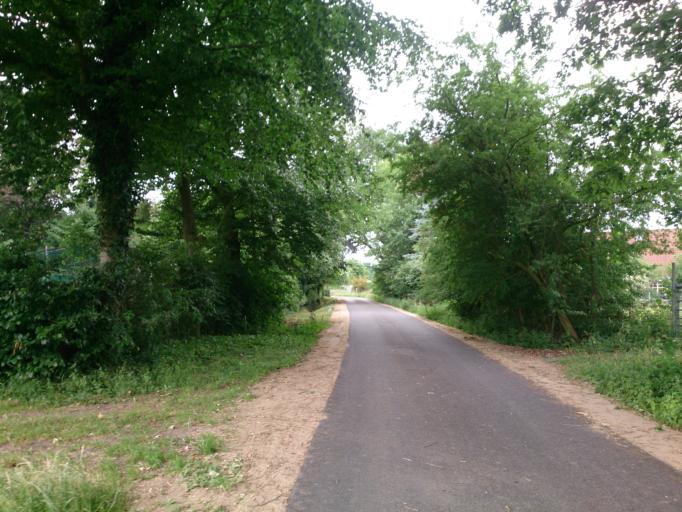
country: DE
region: Schleswig-Holstein
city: Bevern
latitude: 53.7385
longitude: 9.8052
